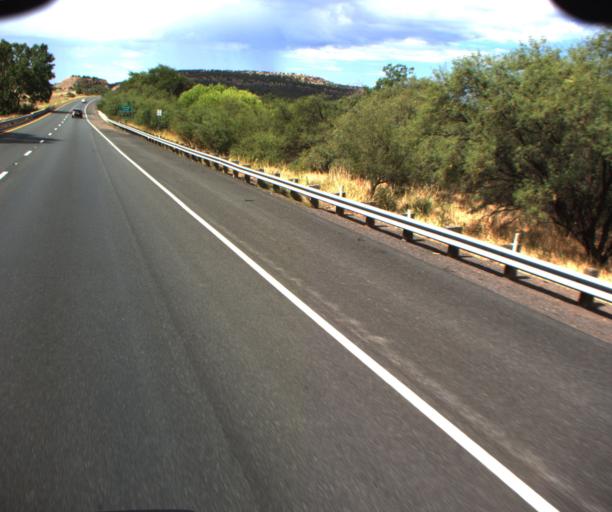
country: US
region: Arizona
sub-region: Yavapai County
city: Camp Verde
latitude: 34.5098
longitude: -111.9958
